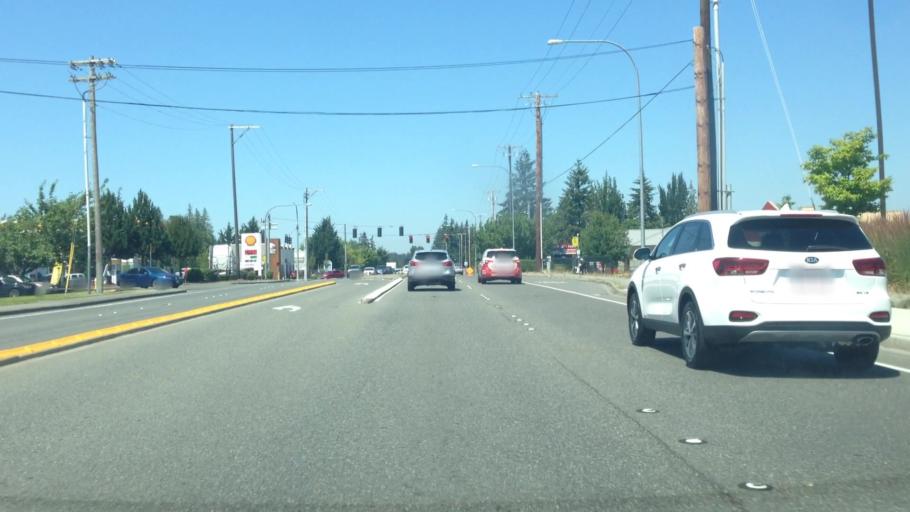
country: US
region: Washington
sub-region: Pierce County
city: Edgewood
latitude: 47.2517
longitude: -122.2938
